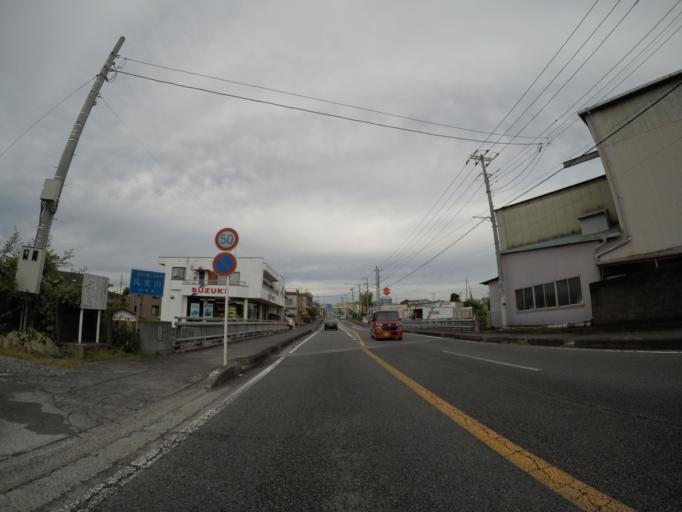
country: JP
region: Shizuoka
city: Fuji
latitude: 35.1888
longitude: 138.6523
